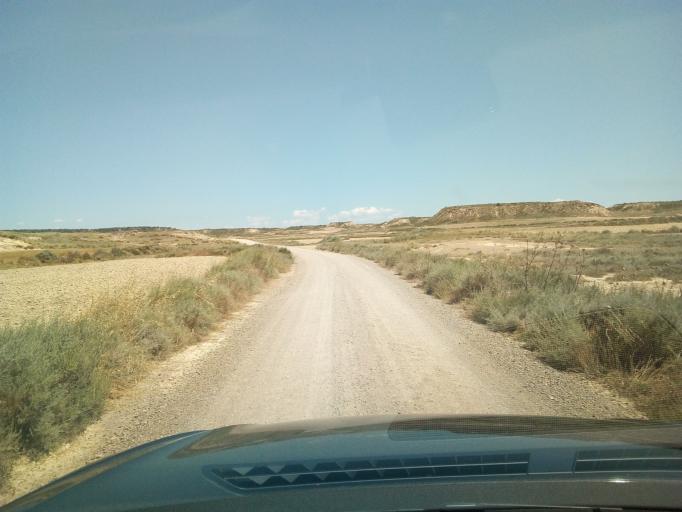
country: ES
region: Aragon
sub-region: Provincia de Zaragoza
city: Sadaba
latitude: 42.1783
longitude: -1.4090
